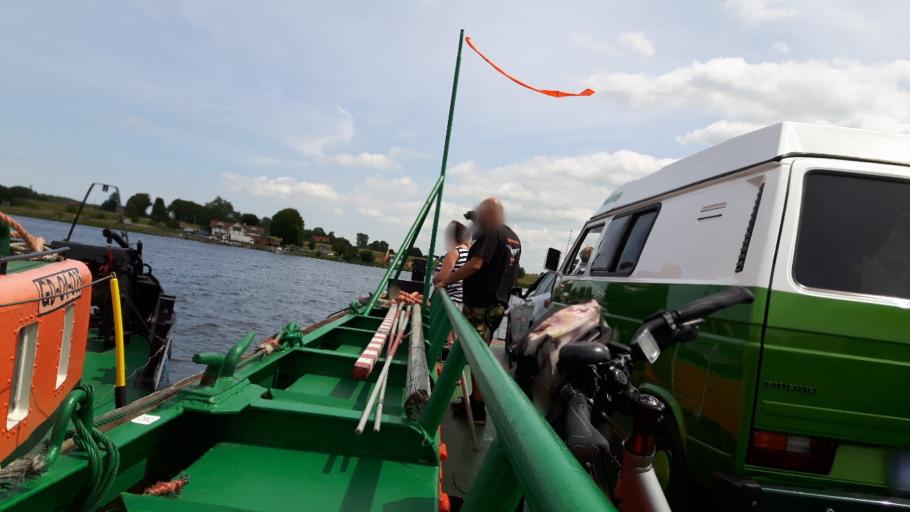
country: PL
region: Pomeranian Voivodeship
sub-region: Powiat nowodworski
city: Ostaszewo
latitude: 54.3331
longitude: 18.9389
